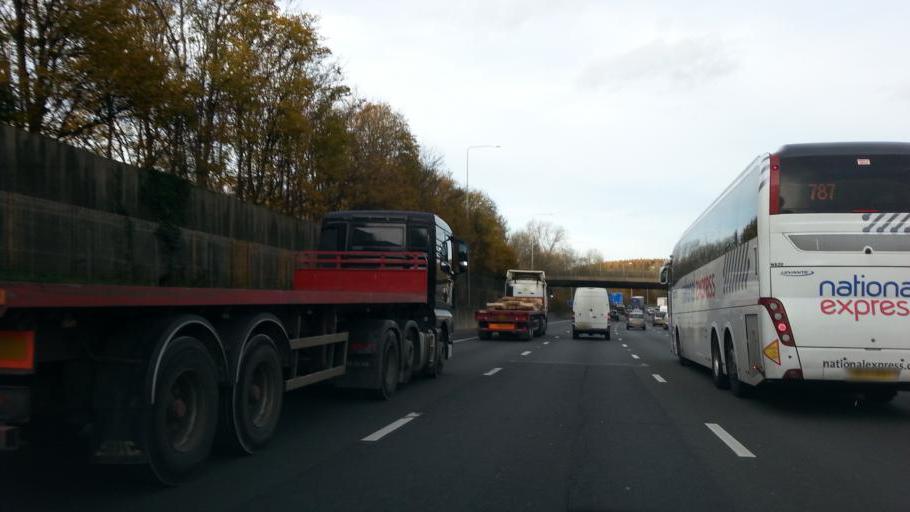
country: GB
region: England
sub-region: Hertfordshire
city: Chorleywood
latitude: 51.6617
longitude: -0.4944
